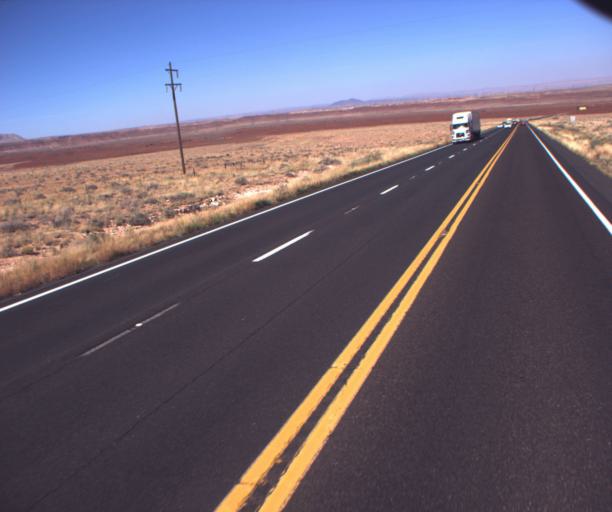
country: US
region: Arizona
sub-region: Coconino County
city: Tuba City
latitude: 35.7658
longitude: -111.4651
